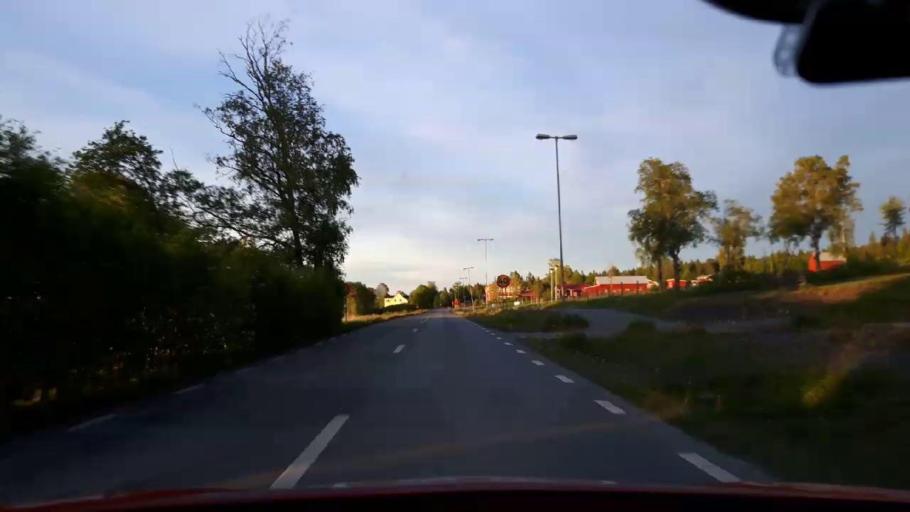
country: SE
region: Jaemtland
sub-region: OEstersunds Kommun
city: Ostersund
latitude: 63.1540
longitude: 14.5644
